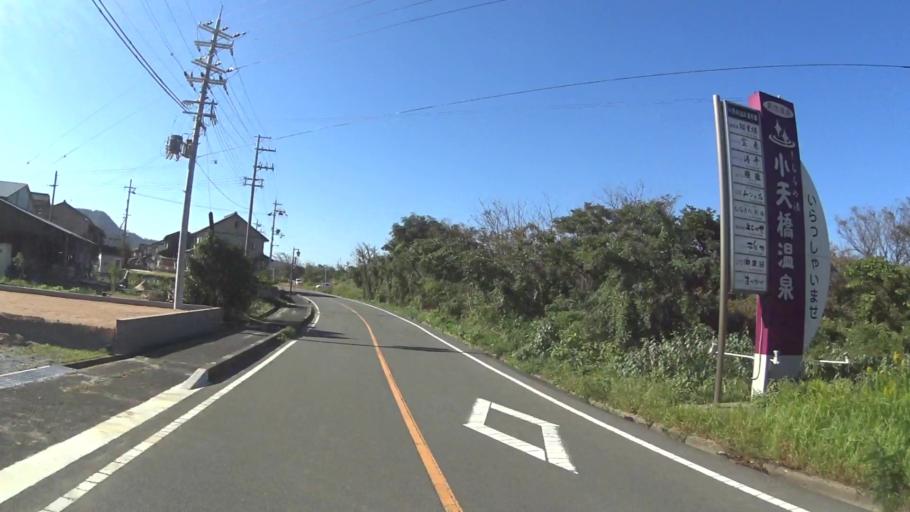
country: JP
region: Hyogo
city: Toyooka
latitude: 35.6432
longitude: 134.9132
